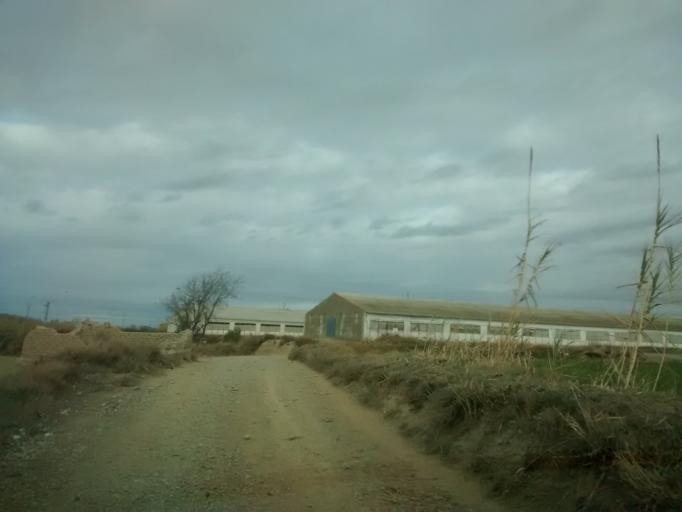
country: ES
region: Aragon
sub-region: Provincia de Zaragoza
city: Villanueva de Gallego
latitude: 41.7096
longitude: -0.8203
